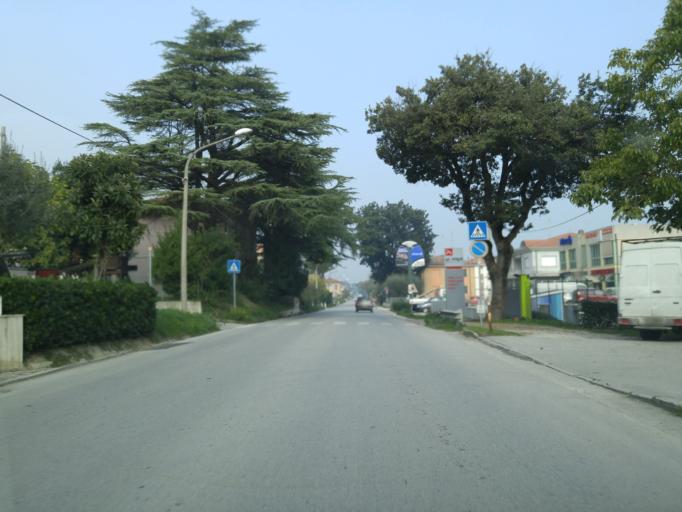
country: IT
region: The Marches
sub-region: Provincia di Pesaro e Urbino
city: Calcinelli
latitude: 43.7571
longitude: 12.9238
